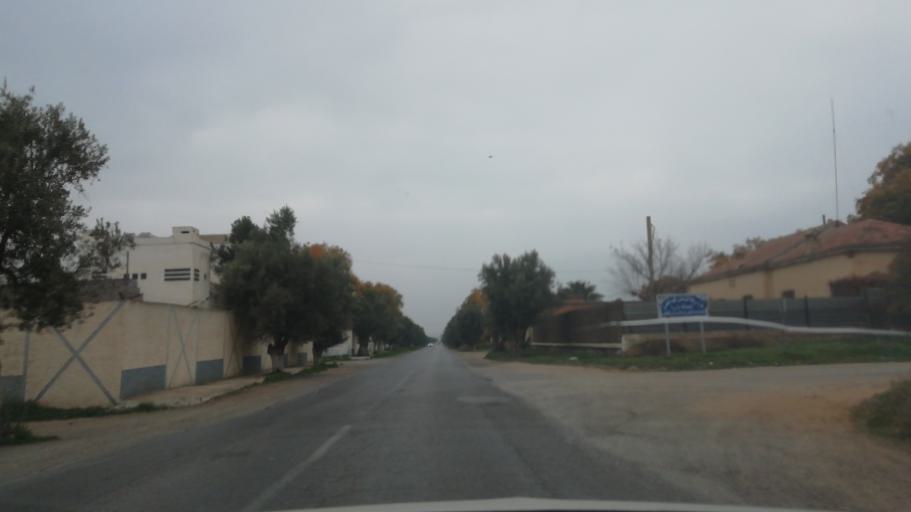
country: DZ
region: Sidi Bel Abbes
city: Sfizef
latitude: 35.2285
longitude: -0.2651
